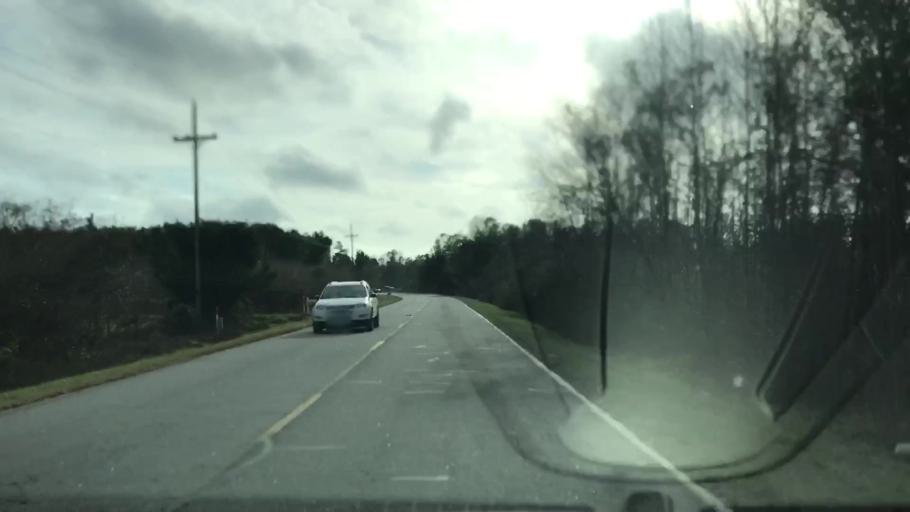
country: US
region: South Carolina
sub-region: Williamsburg County
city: Andrews
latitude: 33.3514
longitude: -79.6603
